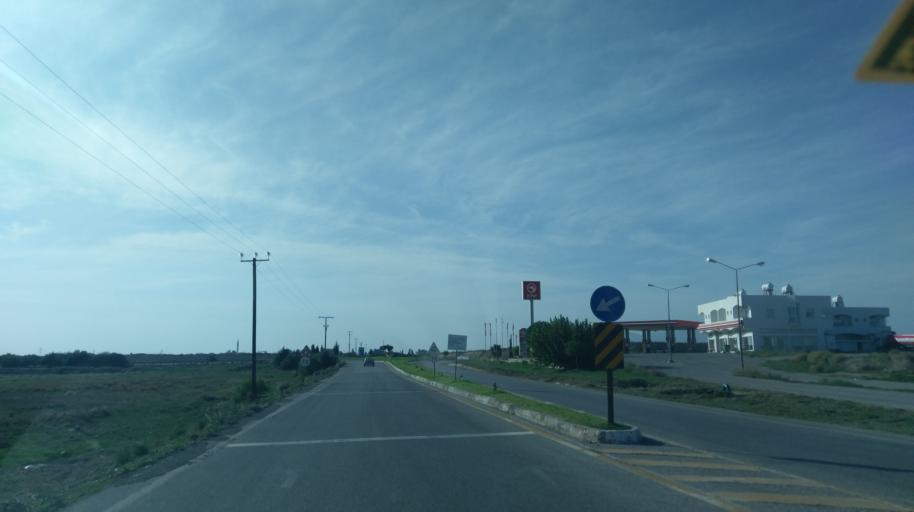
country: CY
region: Ammochostos
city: Lefkonoiko
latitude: 35.2620
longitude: 33.7497
